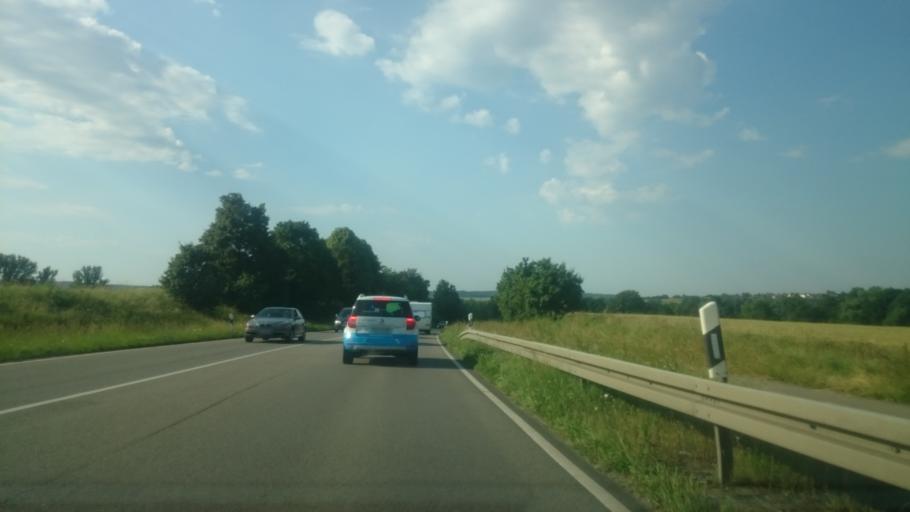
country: DE
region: Baden-Wuerttemberg
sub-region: Tuebingen Region
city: Gomaringen
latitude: 48.4464
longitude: 9.0793
